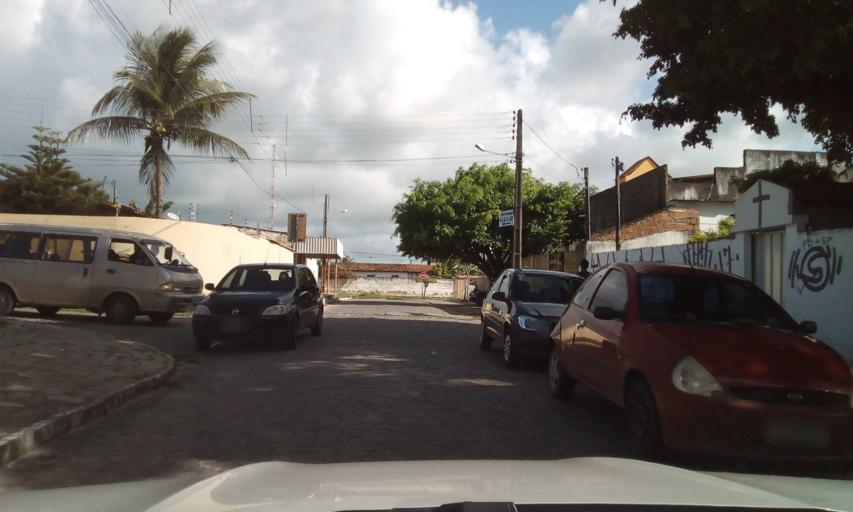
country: BR
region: Paraiba
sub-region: Joao Pessoa
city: Joao Pessoa
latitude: -7.1780
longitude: -34.8812
